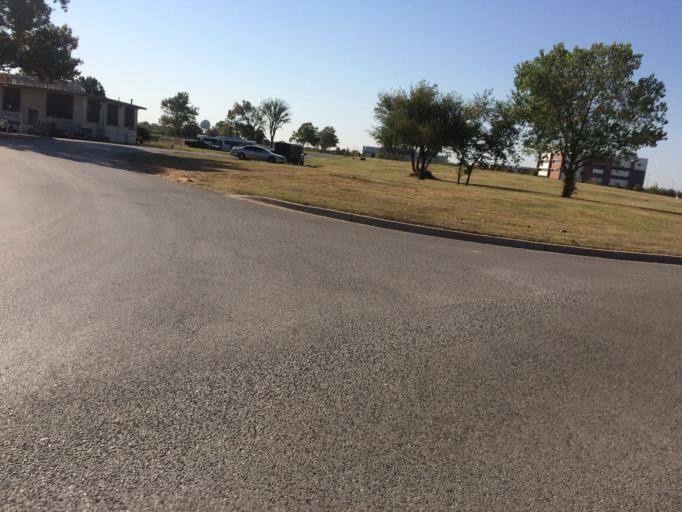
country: US
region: Oklahoma
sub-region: Cleveland County
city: Norman
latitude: 35.1867
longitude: -97.4358
